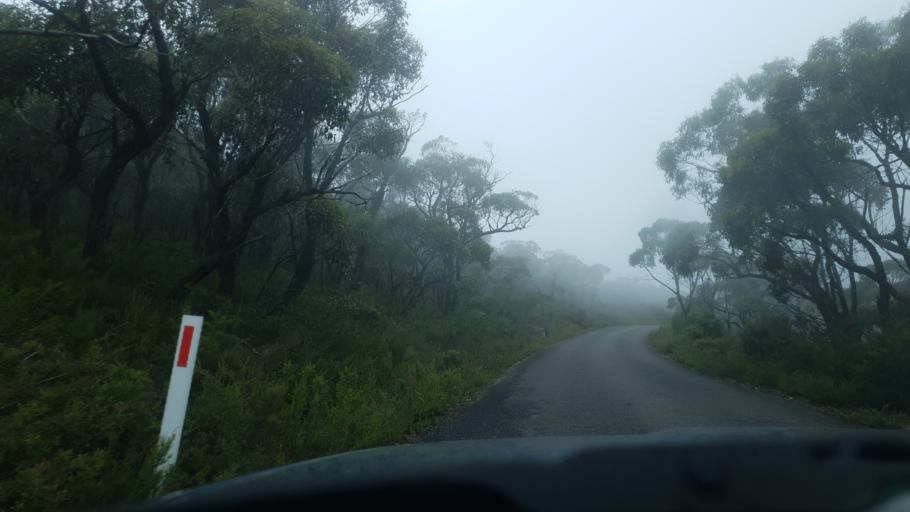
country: AU
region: Victoria
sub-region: Northern Grampians
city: Stawell
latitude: -37.2753
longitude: 142.5835
